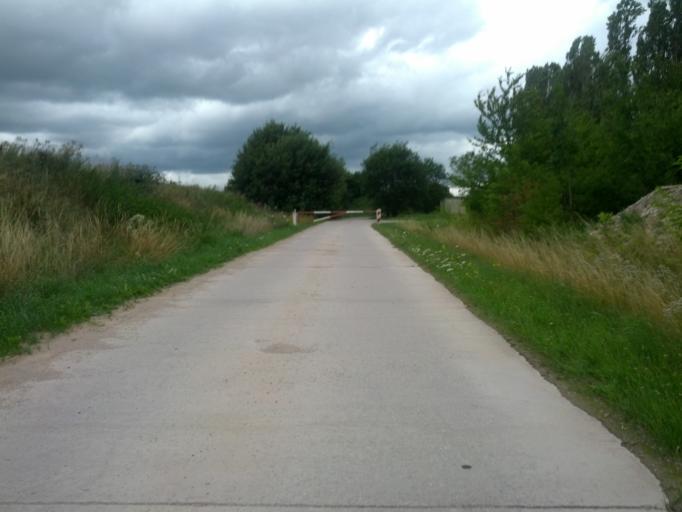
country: DE
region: Thuringia
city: Bischofroda
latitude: 50.9952
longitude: 10.3870
